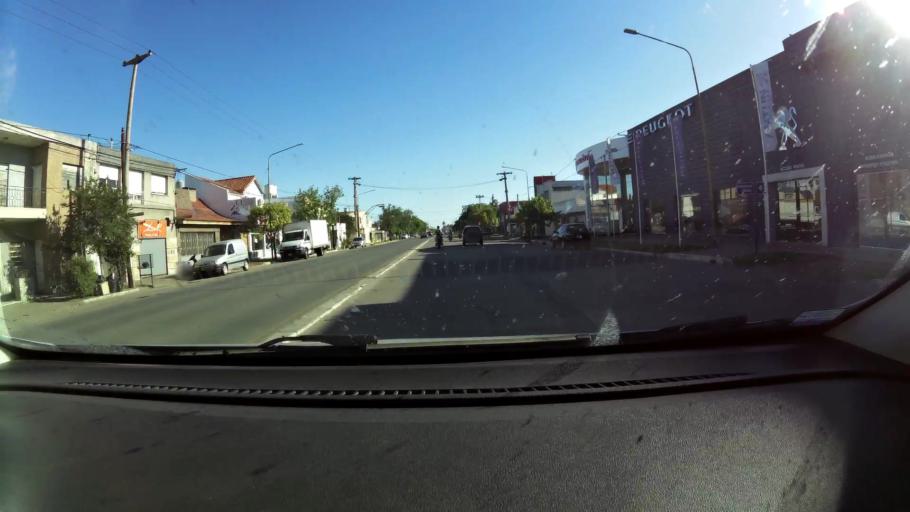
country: AR
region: Cordoba
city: San Francisco
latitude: -31.4241
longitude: -62.0961
